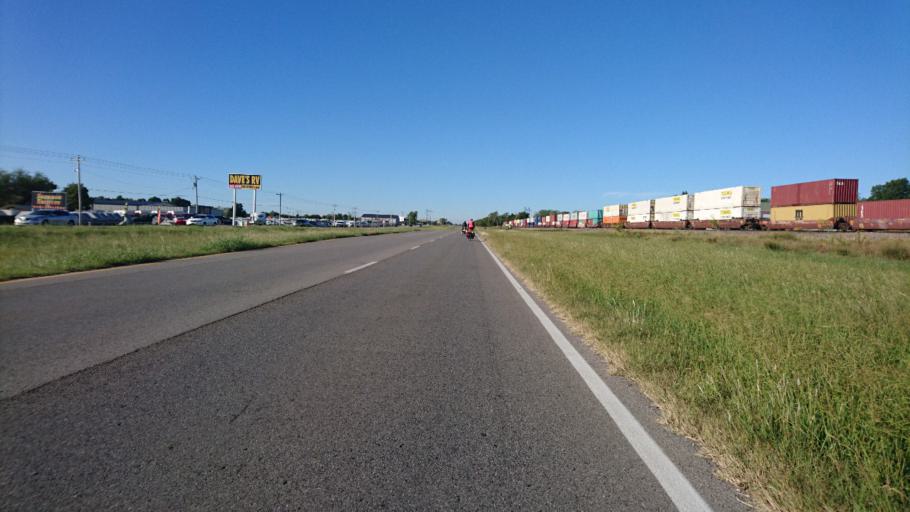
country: US
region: Oklahoma
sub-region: Rogers County
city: Verdigris
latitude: 36.2602
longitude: -95.6574
